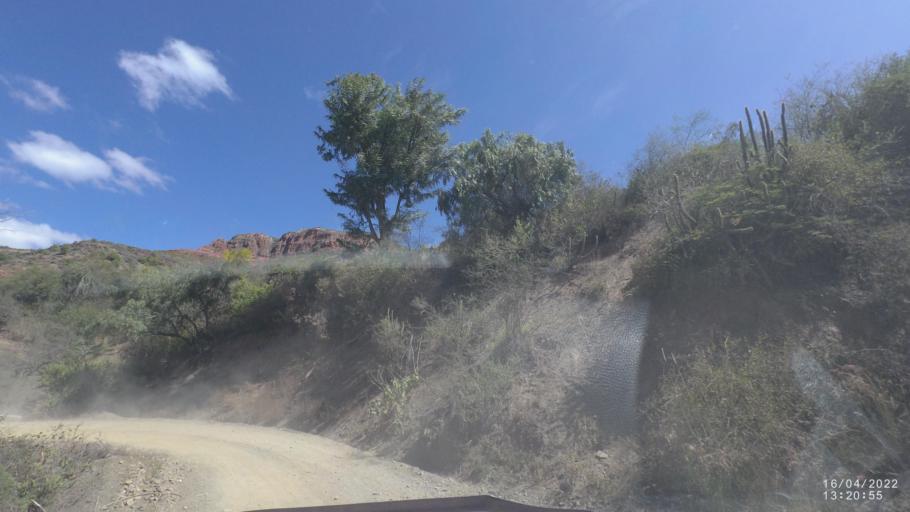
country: BO
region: Cochabamba
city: Mizque
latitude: -17.9910
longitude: -65.6125
